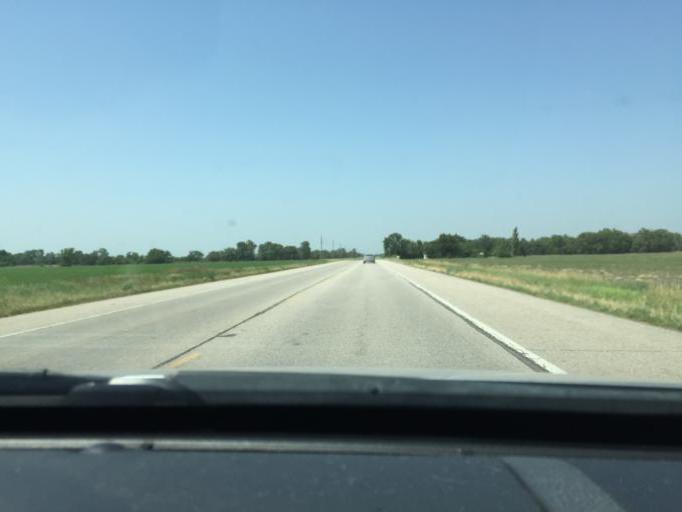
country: US
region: Kansas
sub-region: Reno County
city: South Hutchinson
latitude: 38.0029
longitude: -97.8671
